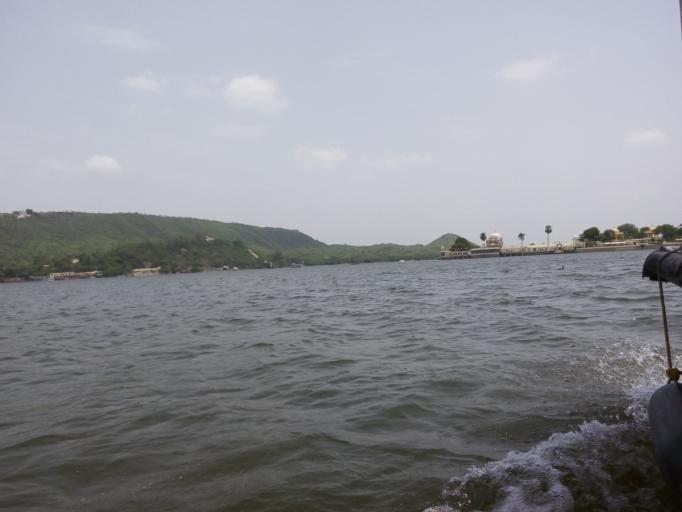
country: IN
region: Rajasthan
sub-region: Udaipur
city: Udaipur
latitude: 24.5717
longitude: 73.6773
